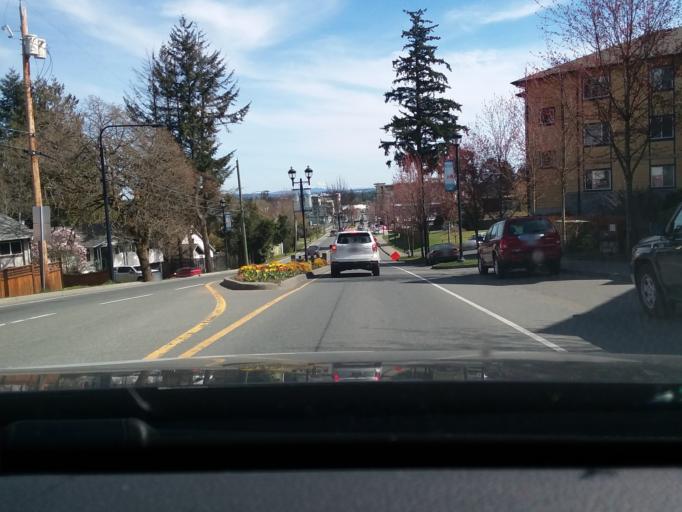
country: CA
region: British Columbia
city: Colwood
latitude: 48.4444
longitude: -123.4751
